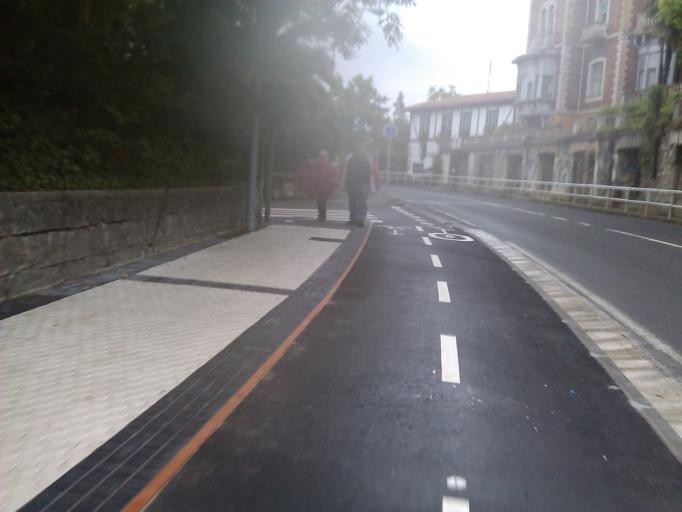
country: ES
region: Basque Country
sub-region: Provincia de Guipuzcoa
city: Astigarraga
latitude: 43.2987
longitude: -1.9559
